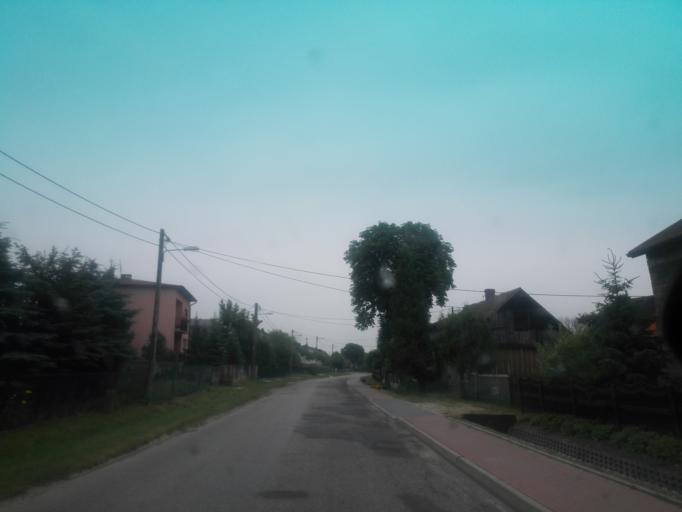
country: PL
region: Silesian Voivodeship
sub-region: Powiat czestochowski
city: Mstow
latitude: 50.7967
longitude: 19.3228
